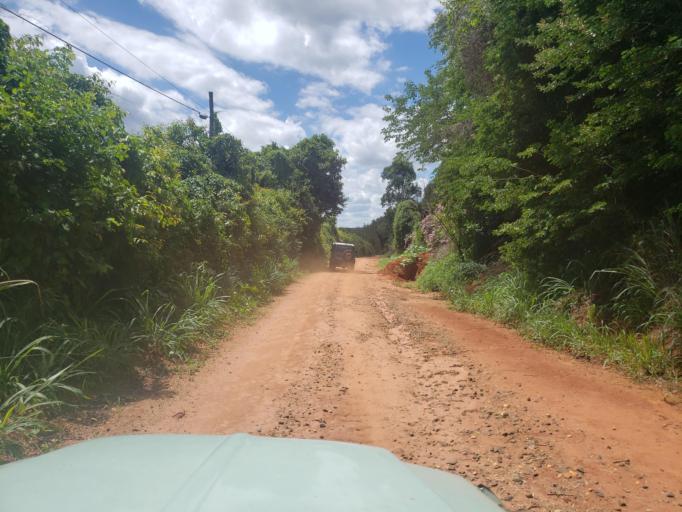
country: BR
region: Sao Paulo
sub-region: Conchal
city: Conchal
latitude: -22.2533
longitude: -47.0771
